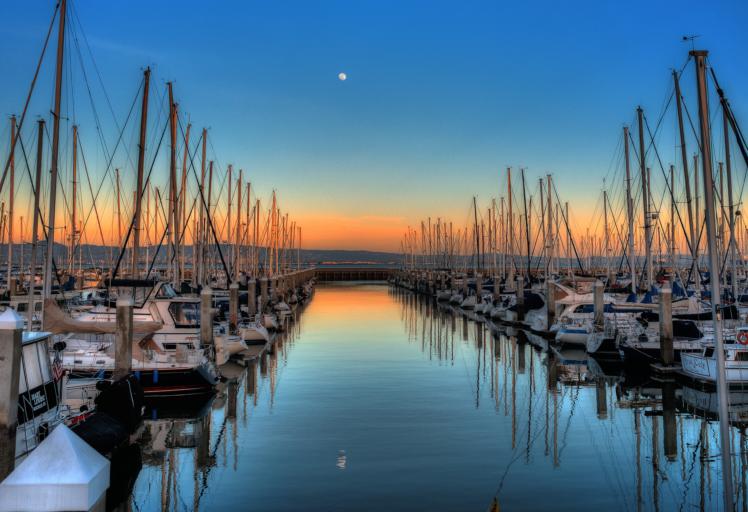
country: US
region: California
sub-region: San Francisco County
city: San Francisco
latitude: 37.7803
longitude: -122.3876
